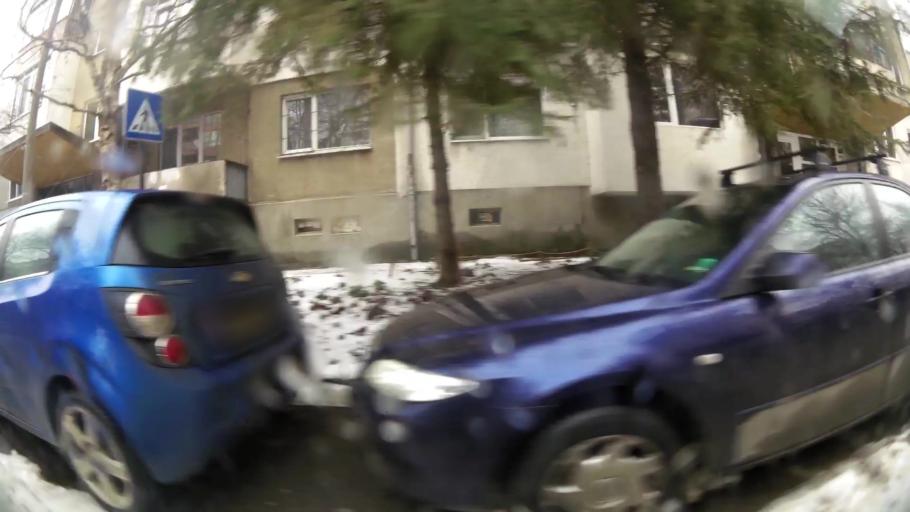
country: BG
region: Sofia-Capital
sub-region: Stolichna Obshtina
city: Sofia
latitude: 42.6723
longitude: 23.2763
